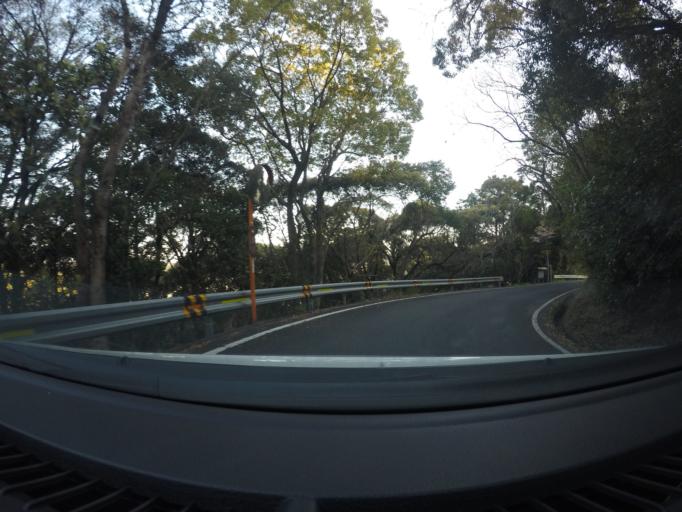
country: JP
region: Kochi
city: Kochi-shi
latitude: 33.5467
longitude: 133.5802
